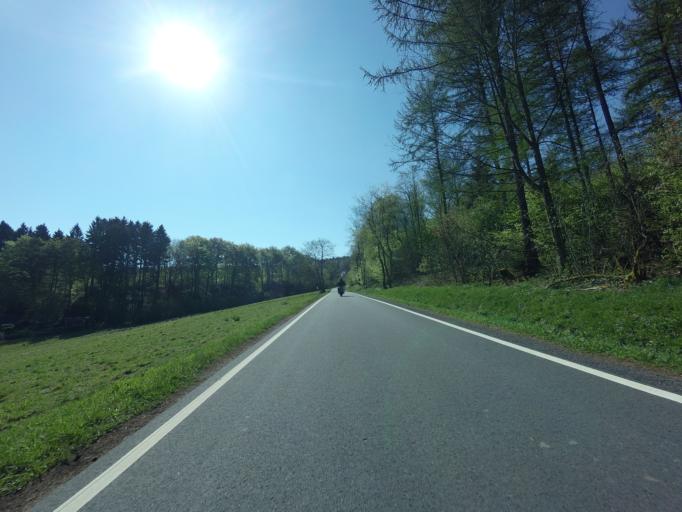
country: DE
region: North Rhine-Westphalia
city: Meinerzhagen
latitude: 51.1322
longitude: 7.6791
